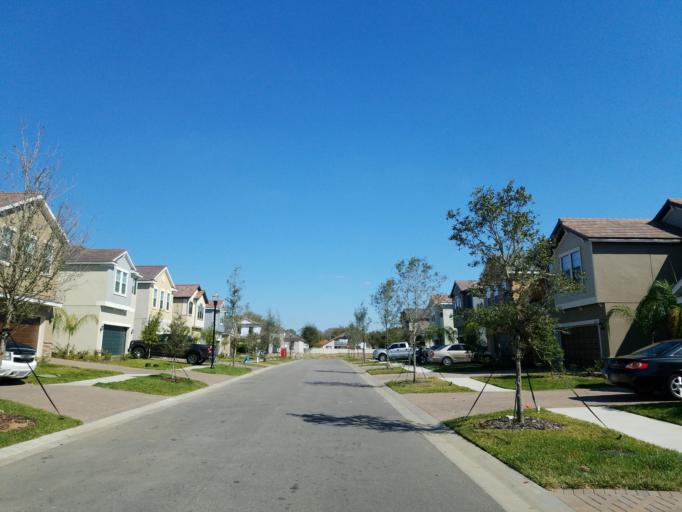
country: US
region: Florida
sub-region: Hillsborough County
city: Brandon
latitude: 27.9256
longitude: -82.2668
